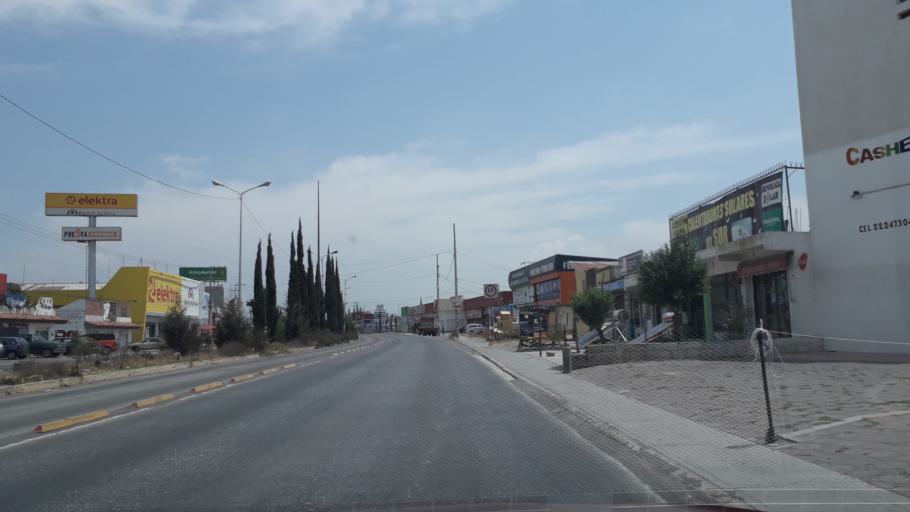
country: MX
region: Puebla
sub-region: Puebla
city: El Capulo (La Quebradora)
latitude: 18.9756
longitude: -98.2578
